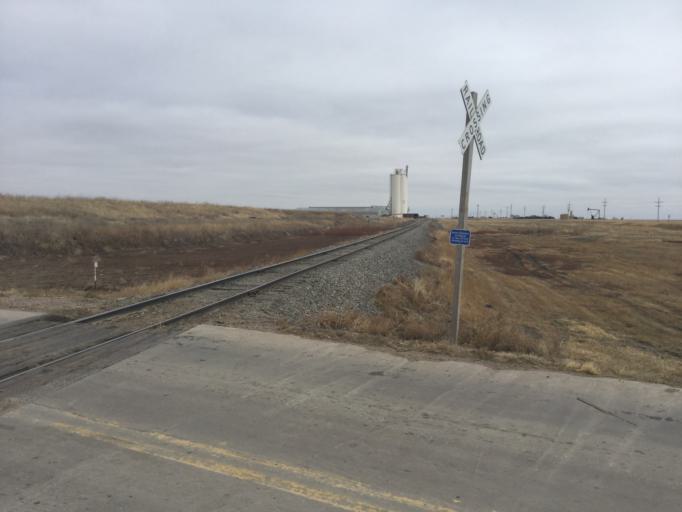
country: US
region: Kansas
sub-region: Haskell County
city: Sublette
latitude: 37.4864
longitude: -100.8347
